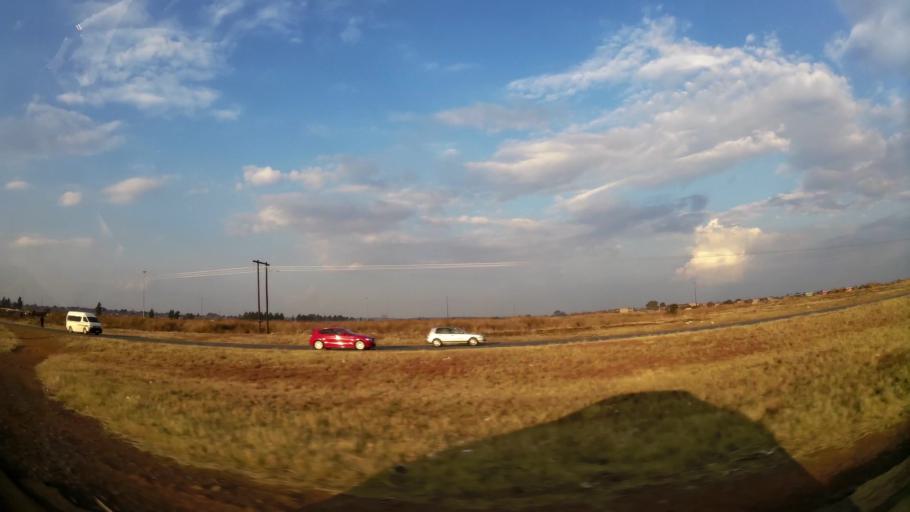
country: ZA
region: Gauteng
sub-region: Sedibeng District Municipality
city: Vanderbijlpark
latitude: -26.5950
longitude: 27.8202
